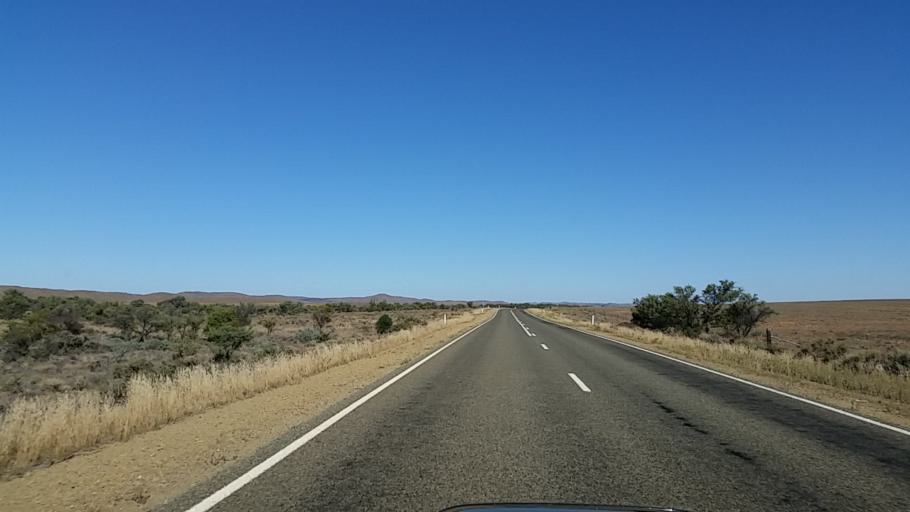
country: AU
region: South Australia
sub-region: Flinders Ranges
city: Quorn
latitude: -32.4002
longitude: 138.5142
